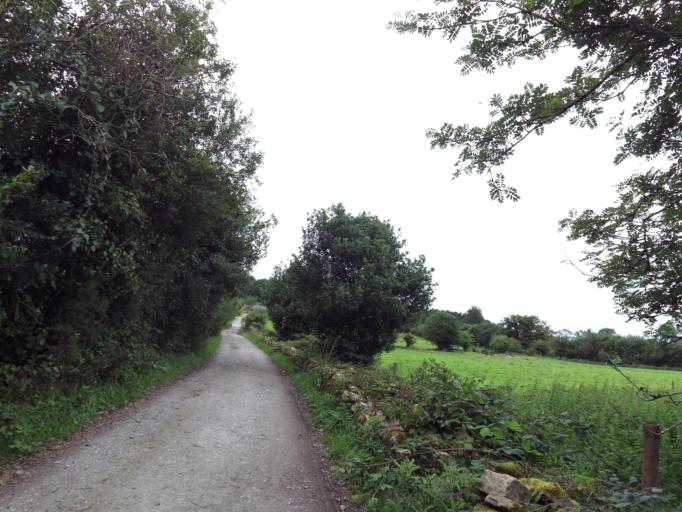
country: IE
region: Connaught
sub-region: County Galway
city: Loughrea
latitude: 53.1317
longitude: -8.4785
